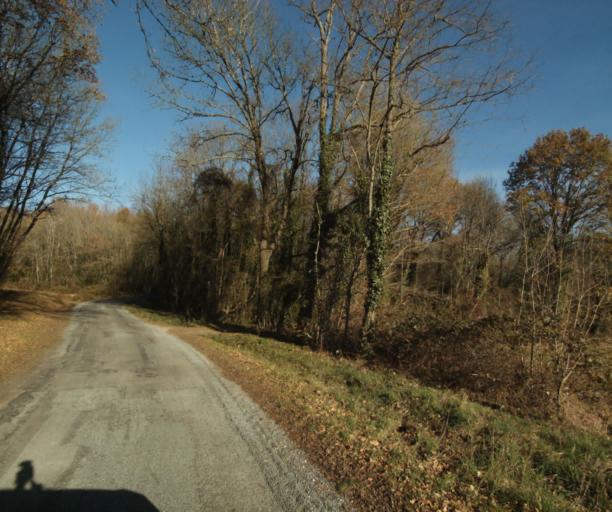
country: FR
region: Poitou-Charentes
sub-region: Departement de la Charente-Maritime
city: Ecoyeux
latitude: 45.7614
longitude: -0.5088
